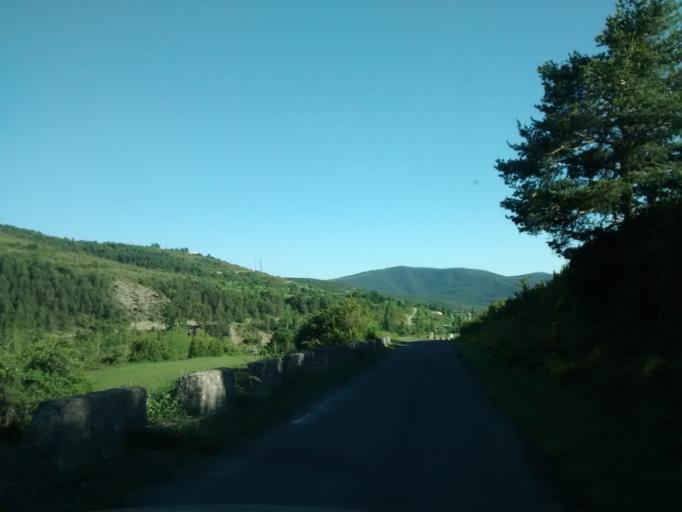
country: ES
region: Aragon
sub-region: Provincia de Huesca
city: Jasa
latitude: 42.6920
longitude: -0.6215
